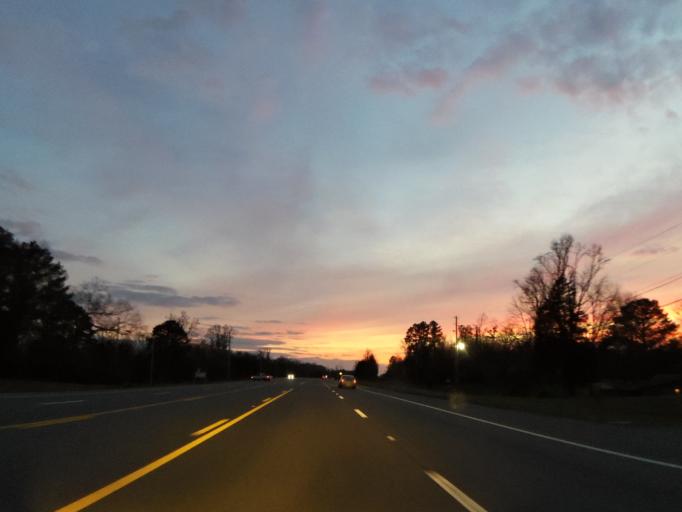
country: US
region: Tennessee
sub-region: Polk County
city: Benton
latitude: 35.1513
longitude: -84.7049
